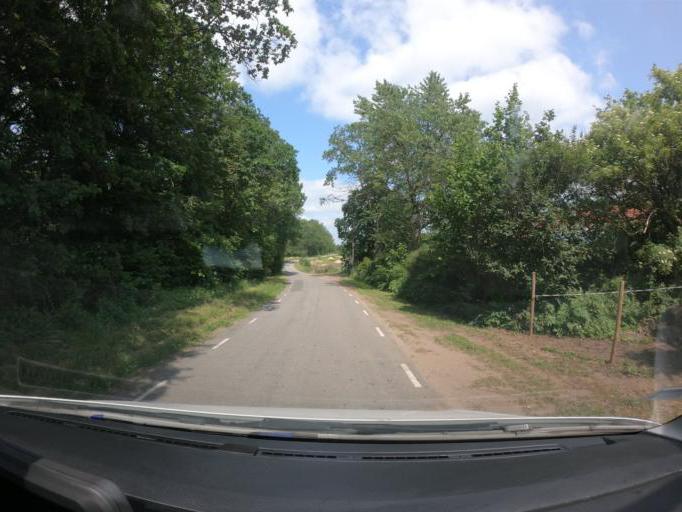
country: SE
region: Skane
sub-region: Hassleholms Kommun
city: Sosdala
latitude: 56.0334
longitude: 13.6470
